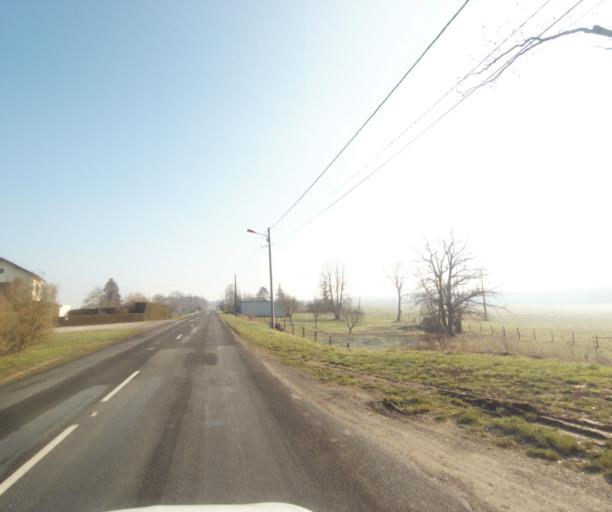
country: FR
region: Champagne-Ardenne
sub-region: Departement de la Haute-Marne
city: Laneuville-a-Remy
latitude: 48.4934
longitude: 4.8626
